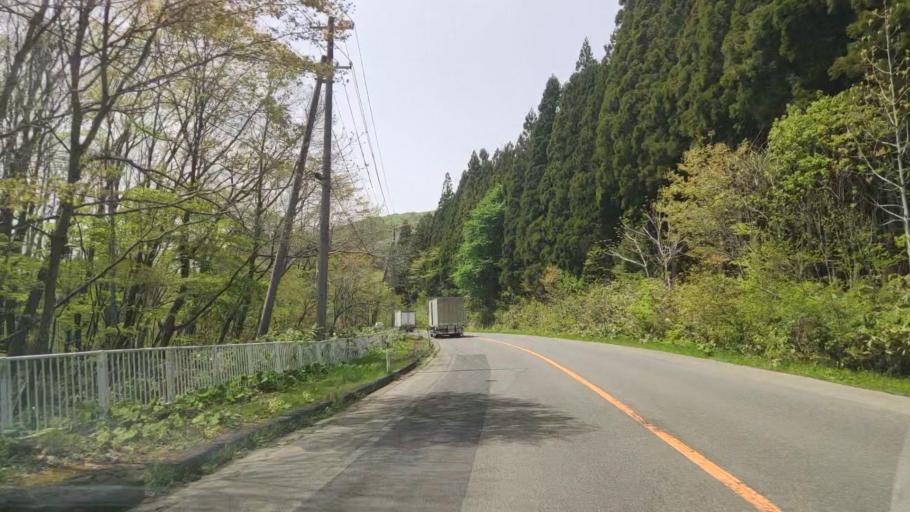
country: JP
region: Aomori
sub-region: Misawa Shi
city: Inuotose
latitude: 40.7911
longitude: 141.0957
